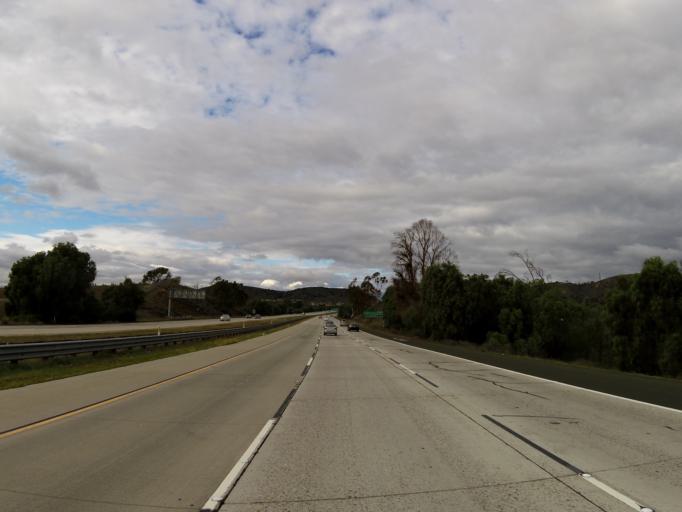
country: US
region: California
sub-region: Ventura County
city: Moorpark
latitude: 34.2592
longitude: -118.8429
